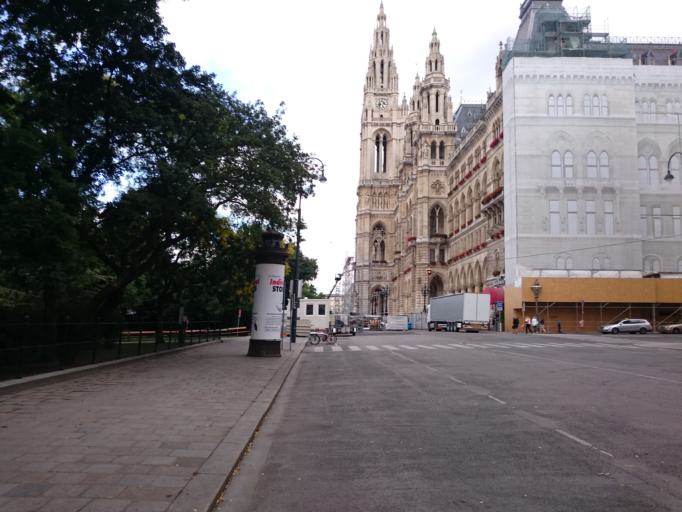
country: AT
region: Vienna
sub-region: Wien Stadt
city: Vienna
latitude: 48.2118
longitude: 16.3588
